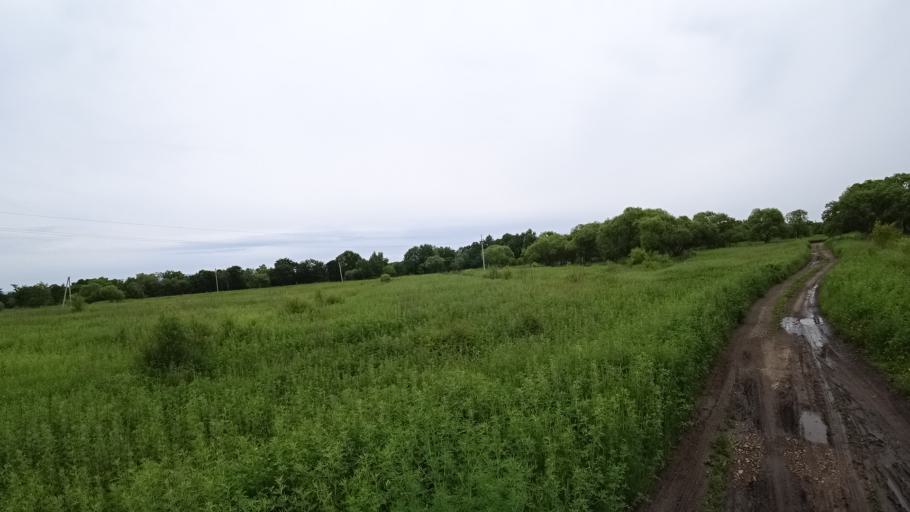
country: RU
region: Primorskiy
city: Novosysoyevka
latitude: 44.2079
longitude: 133.3274
